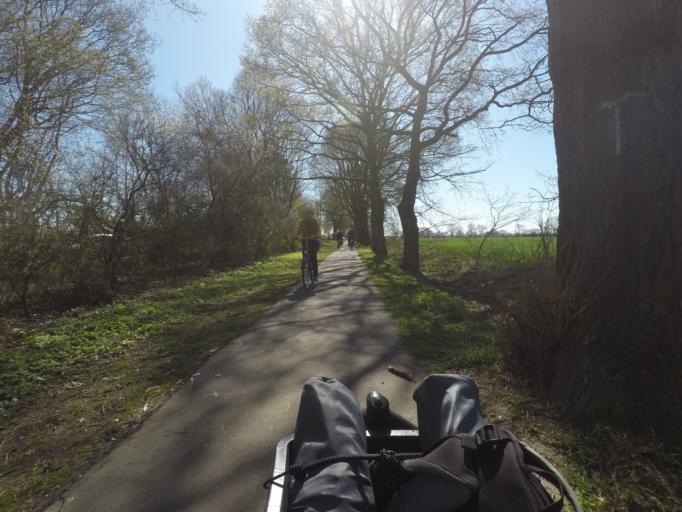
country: DE
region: Schleswig-Holstein
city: Braak
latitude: 53.5991
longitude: 10.2728
